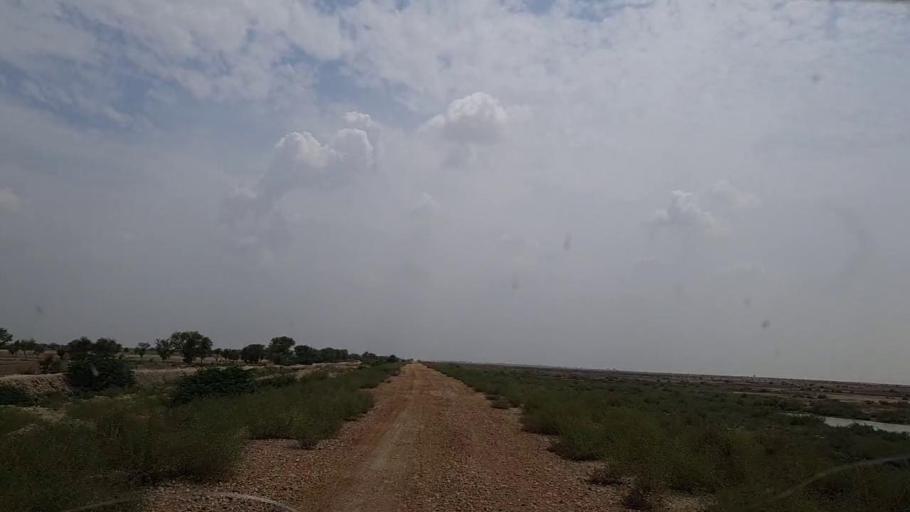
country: PK
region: Sindh
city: Johi
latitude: 26.8018
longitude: 67.6032
